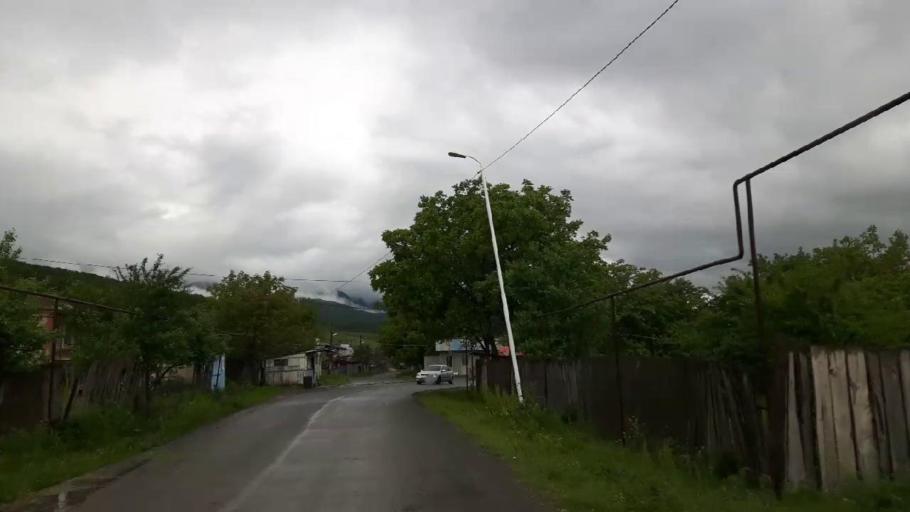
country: GE
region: Shida Kartli
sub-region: Khashuris Raioni
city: Khashuri
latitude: 41.9840
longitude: 43.6641
